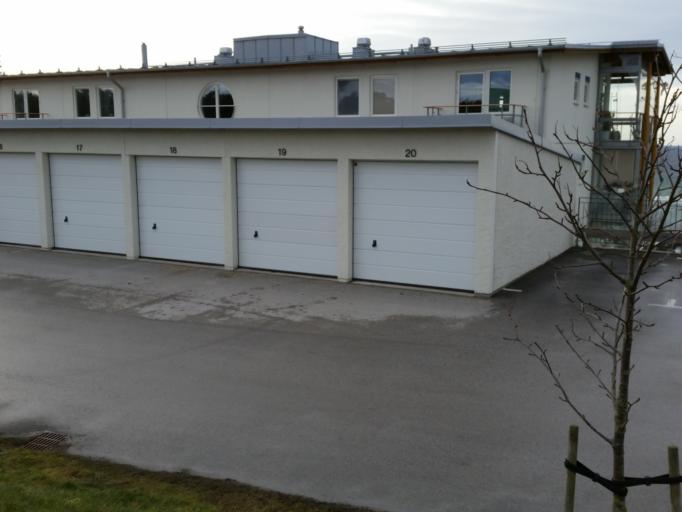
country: SE
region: Gotland
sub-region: Gotland
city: Visby
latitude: 57.6702
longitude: 18.3353
